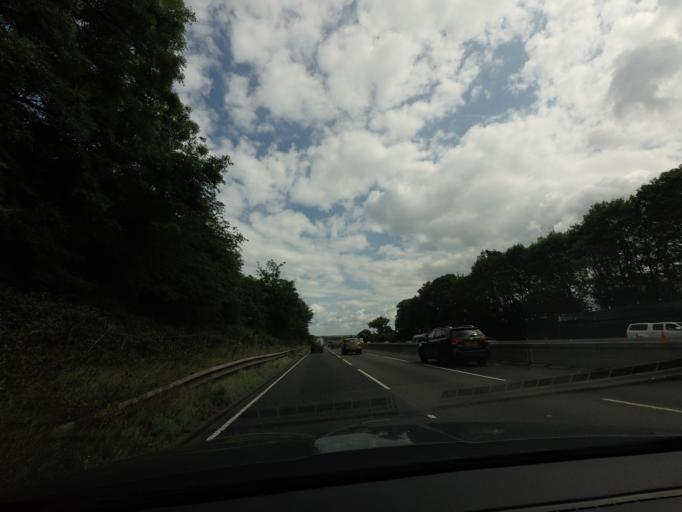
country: GB
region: England
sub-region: Staffordshire
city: Stafford
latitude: 52.7868
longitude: -2.1361
